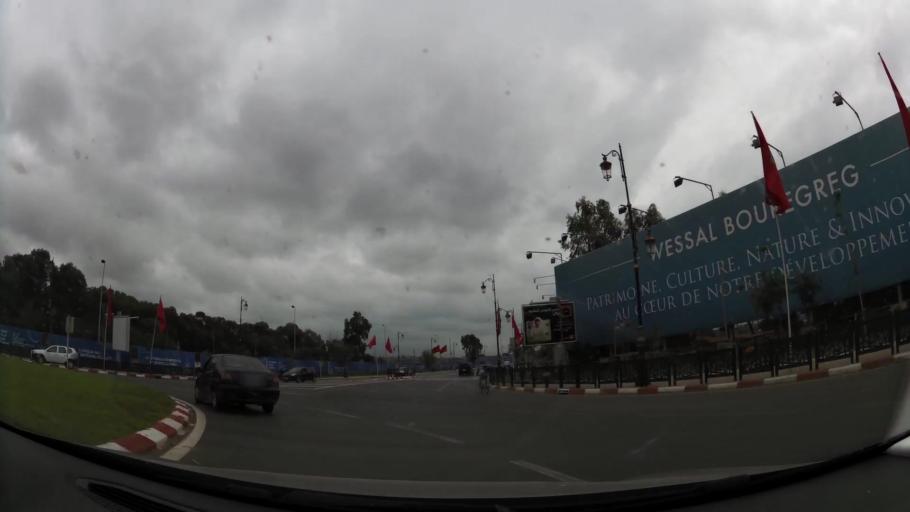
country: MA
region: Rabat-Sale-Zemmour-Zaer
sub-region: Rabat
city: Rabat
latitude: 34.0219
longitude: -6.8031
